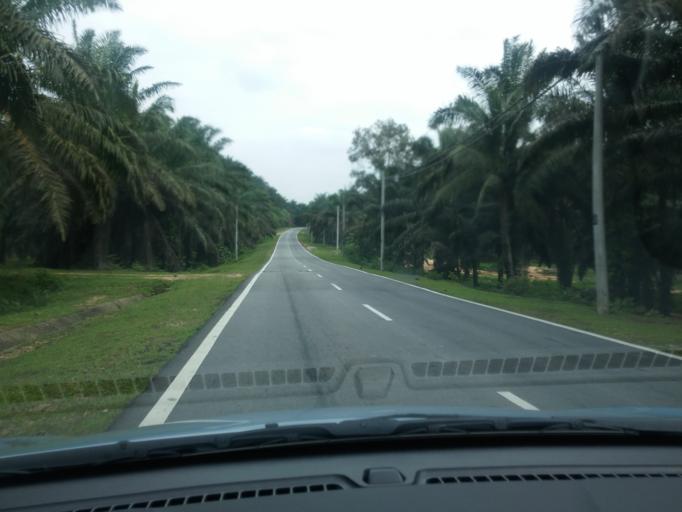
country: MY
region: Pahang
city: Kuantan
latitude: 3.8519
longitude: 103.1626
